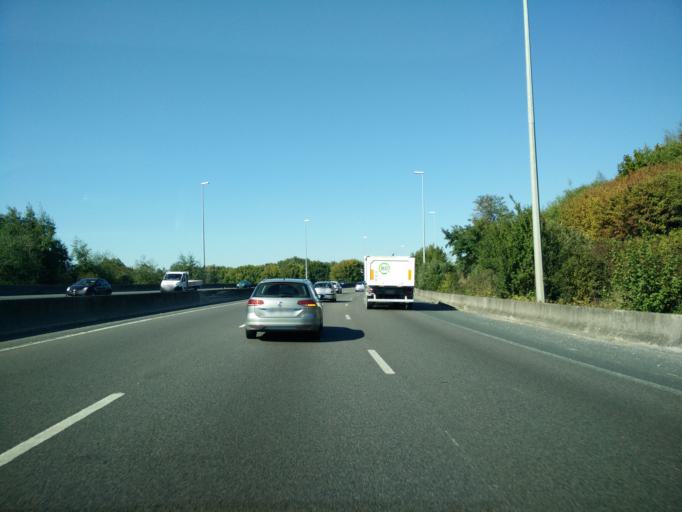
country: FR
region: Ile-de-France
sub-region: Departement de Seine-Saint-Denis
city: Villepinte
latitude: 48.9590
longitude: 2.5264
